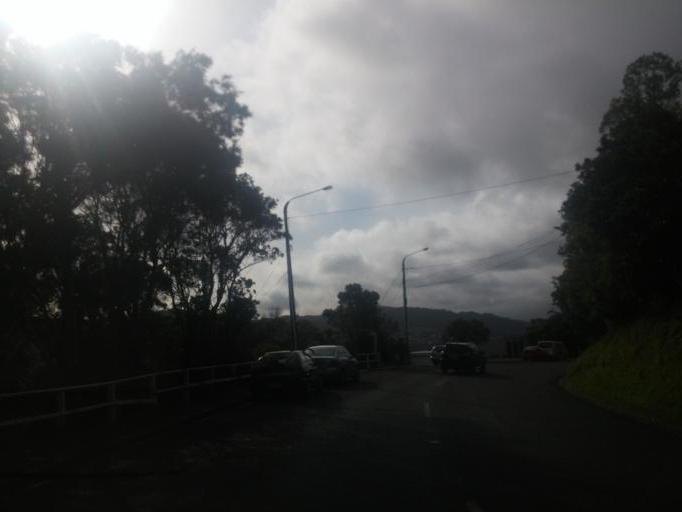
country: NZ
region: Wellington
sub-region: Wellington City
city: Kelburn
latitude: -41.2726
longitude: 174.7578
